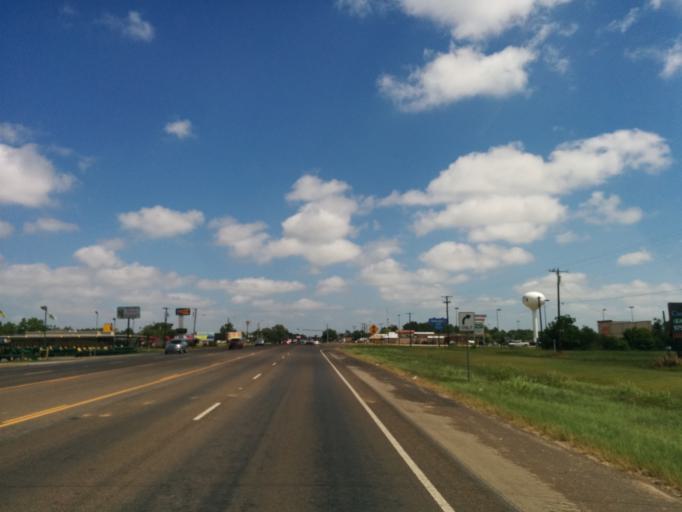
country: US
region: Texas
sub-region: Houston County
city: Crockett
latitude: 31.3177
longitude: -95.4366
